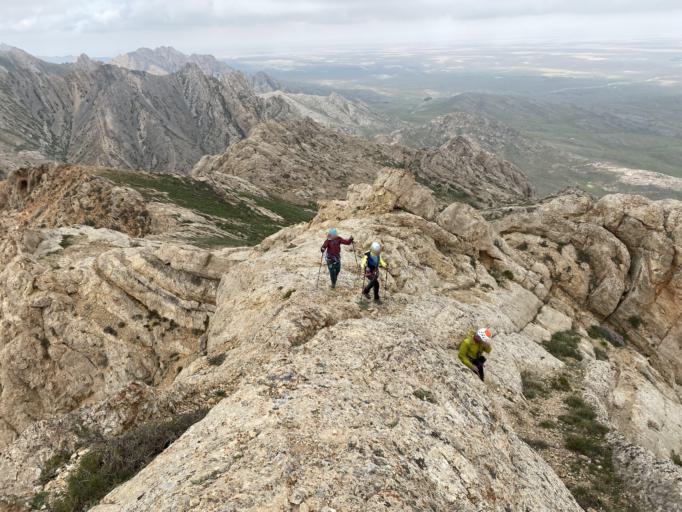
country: KZ
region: Ongtustik Qazaqstan
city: Ashchysay
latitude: 43.7448
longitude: 68.8355
